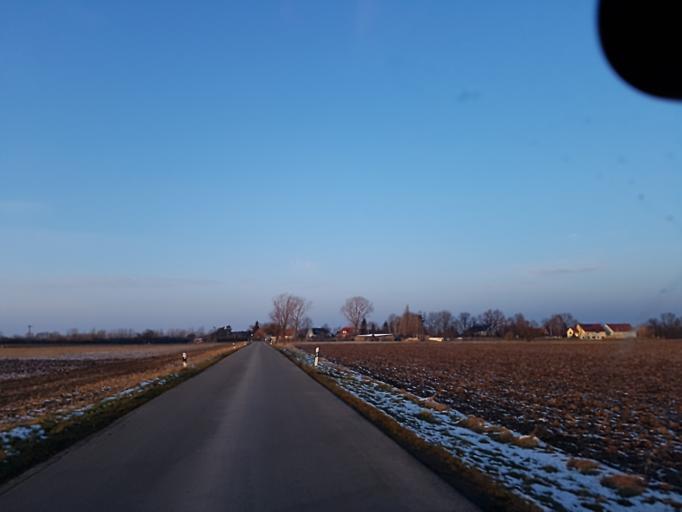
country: DE
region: Saxony
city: Strehla
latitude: 51.3886
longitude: 13.2254
